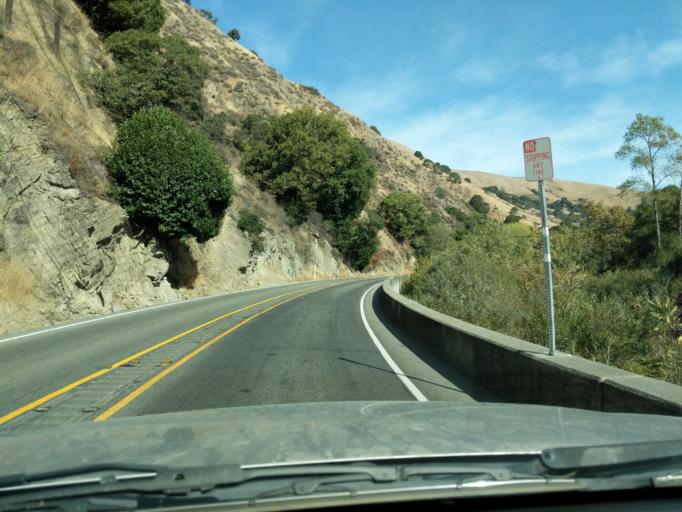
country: US
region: California
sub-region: Alameda County
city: Fremont
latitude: 37.5975
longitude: -121.9516
